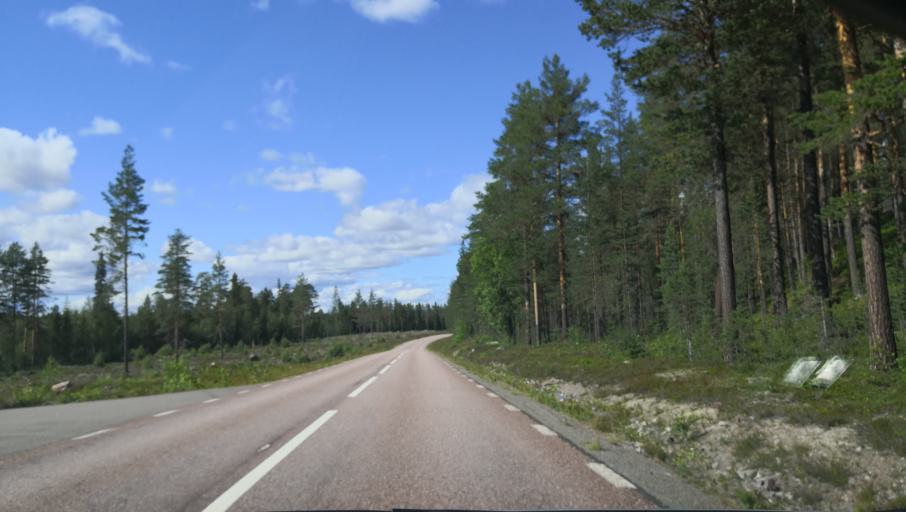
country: NO
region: Hedmark
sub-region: Trysil
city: Innbygda
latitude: 61.7759
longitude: 12.9457
